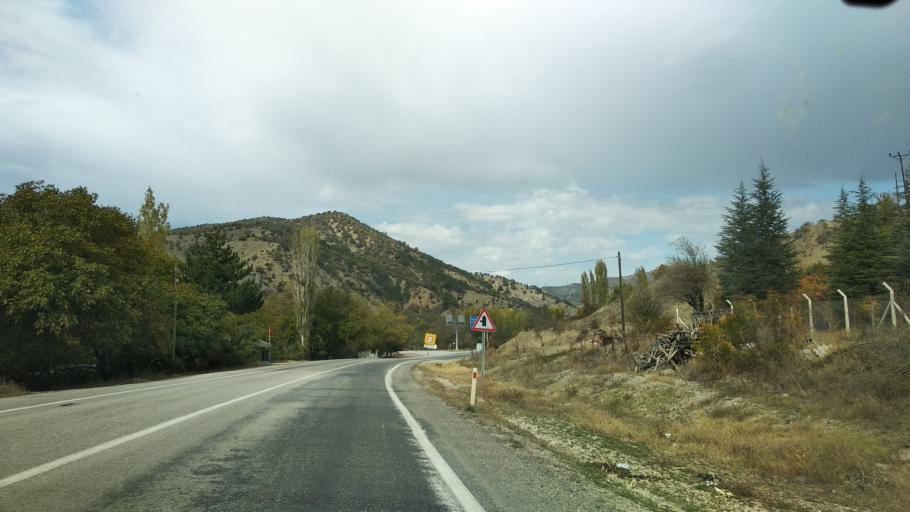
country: TR
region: Ankara
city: Nallihan
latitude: 40.3100
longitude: 31.2692
